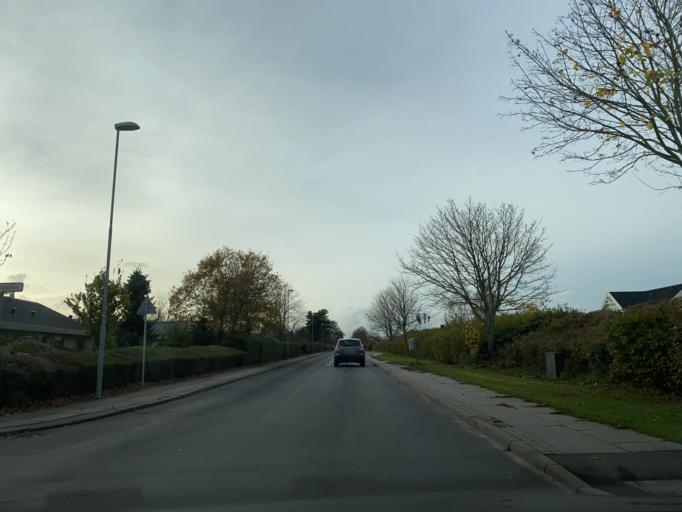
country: DK
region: Central Jutland
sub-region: Skanderborg Kommune
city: Skovby
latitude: 56.1591
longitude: 9.9572
